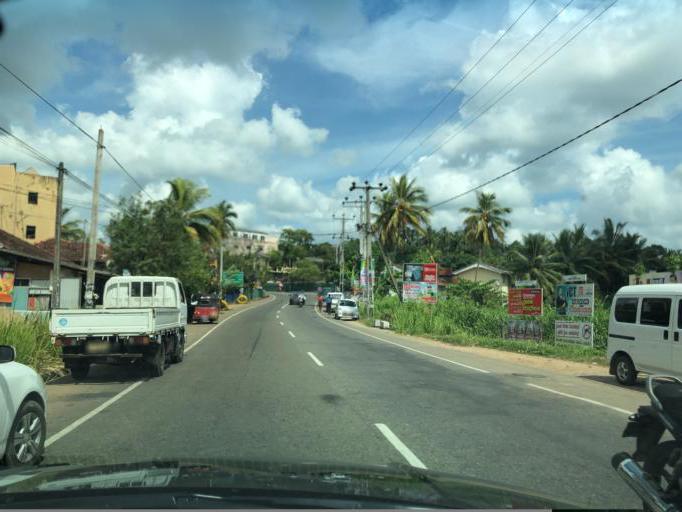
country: LK
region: Western
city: Horawala Junction
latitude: 6.5226
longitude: 80.1103
